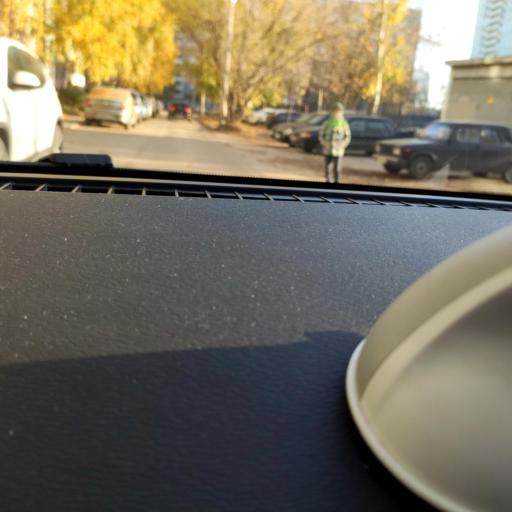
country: RU
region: Samara
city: Samara
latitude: 53.2570
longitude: 50.2162
